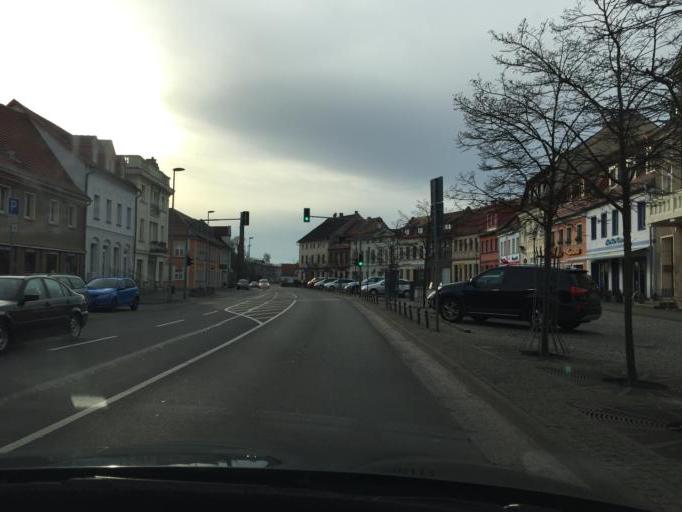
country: DE
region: Brandenburg
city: Peitz
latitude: 51.8582
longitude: 14.4114
